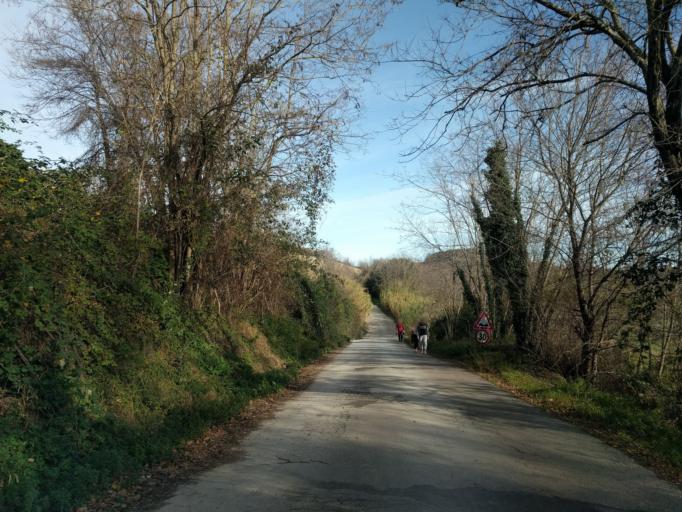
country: IT
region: The Marches
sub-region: Provincia di Pesaro e Urbino
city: Cuccurano
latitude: 43.8094
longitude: 12.9630
